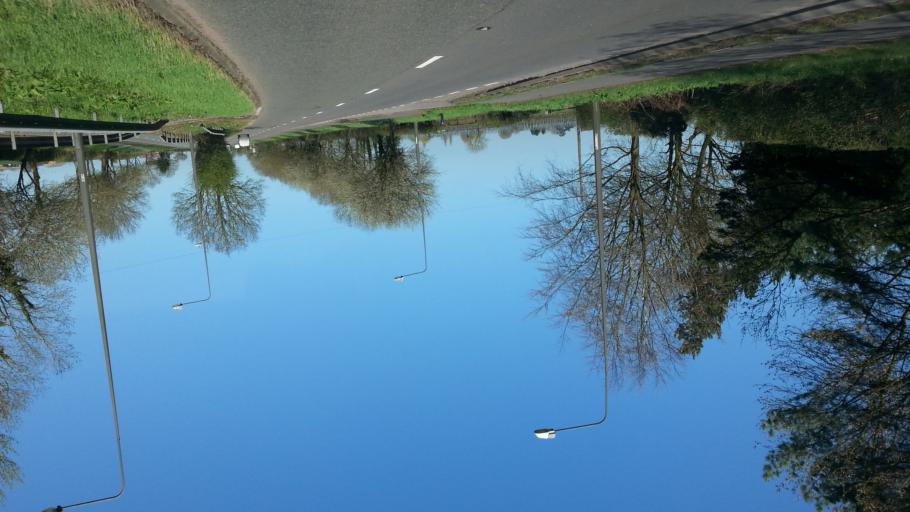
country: GB
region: England
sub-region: Staffordshire
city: Brewood
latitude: 52.6867
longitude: -2.1337
